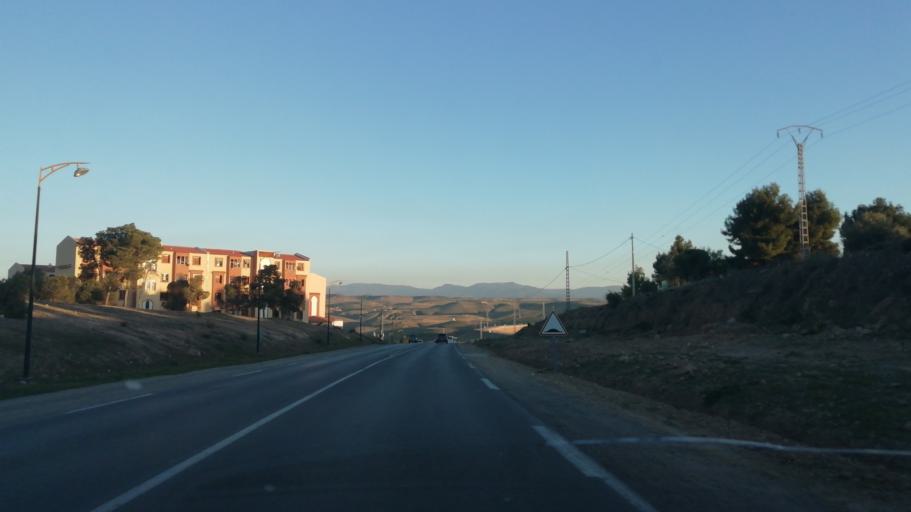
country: DZ
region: Tlemcen
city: Nedroma
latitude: 34.8902
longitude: -1.6543
